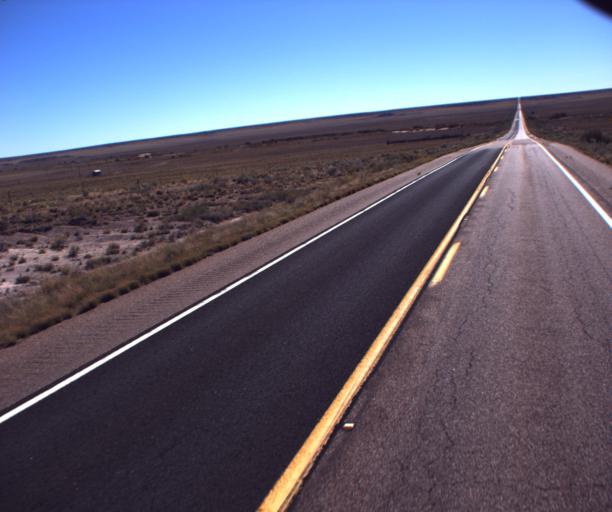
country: US
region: Arizona
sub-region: Navajo County
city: Snowflake
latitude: 34.7500
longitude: -109.8013
